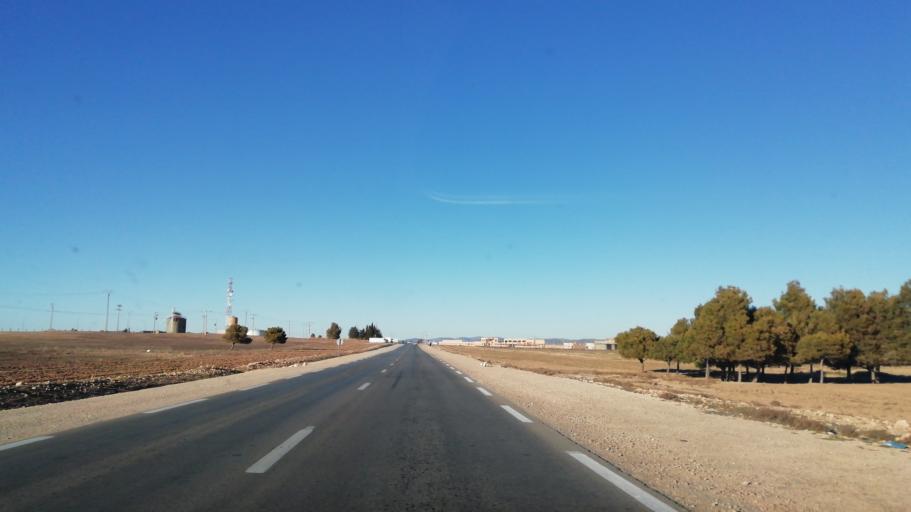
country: DZ
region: Tlemcen
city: Sebdou
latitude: 34.4752
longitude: -1.2714
